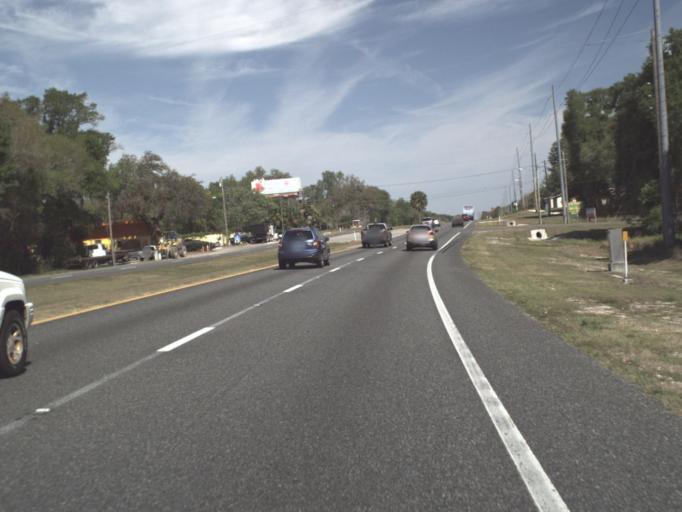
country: US
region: Florida
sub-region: Lake County
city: Lady Lake
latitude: 28.9028
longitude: -81.9141
